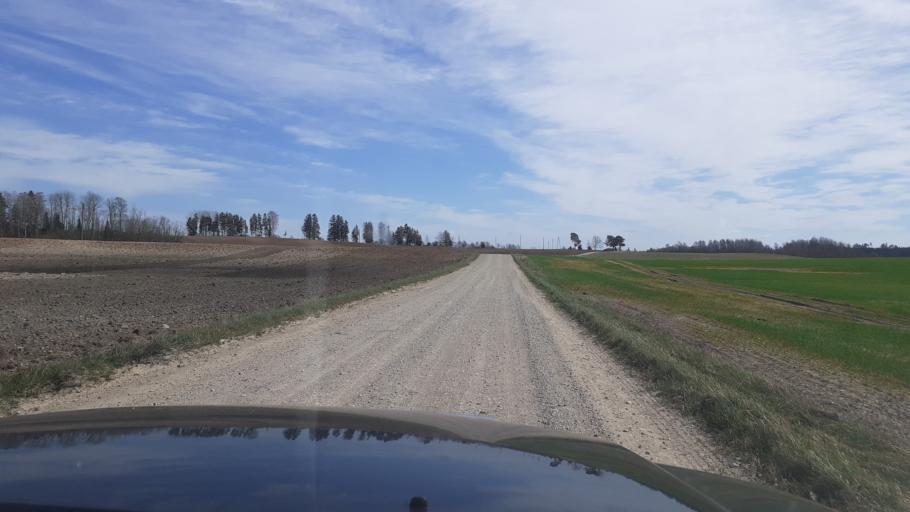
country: LV
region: Kuldigas Rajons
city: Kuldiga
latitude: 56.8422
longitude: 21.9846
